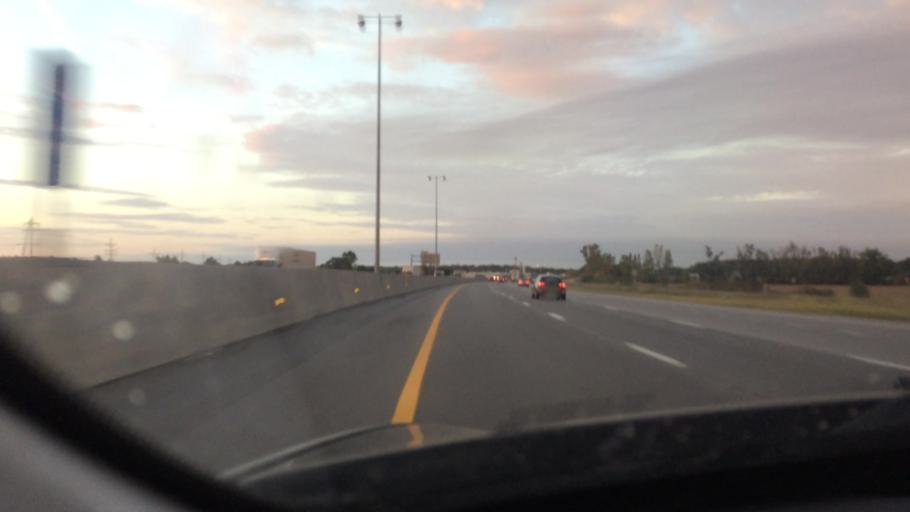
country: US
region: Ohio
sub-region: Wood County
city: North Baltimore
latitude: 41.1678
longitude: -83.6500
